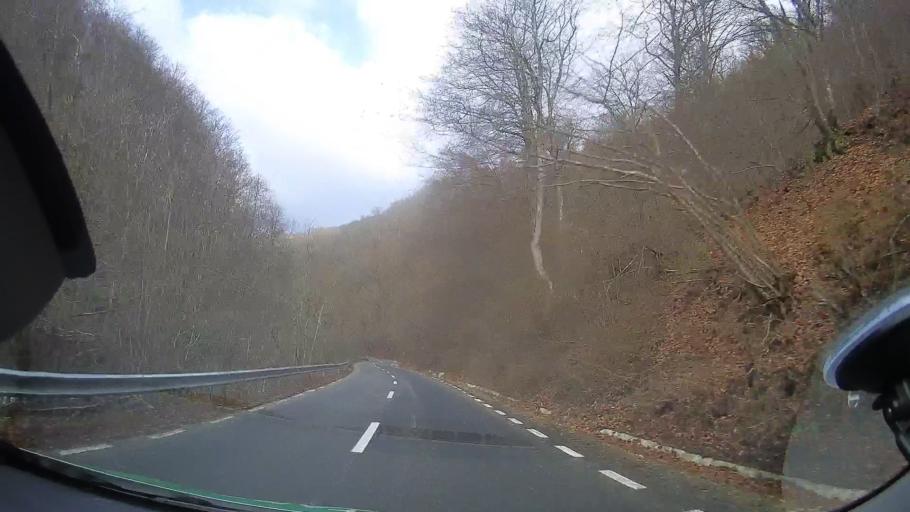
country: RO
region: Cluj
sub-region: Comuna Valea Ierii
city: Valea Ierii
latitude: 46.6344
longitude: 23.3722
